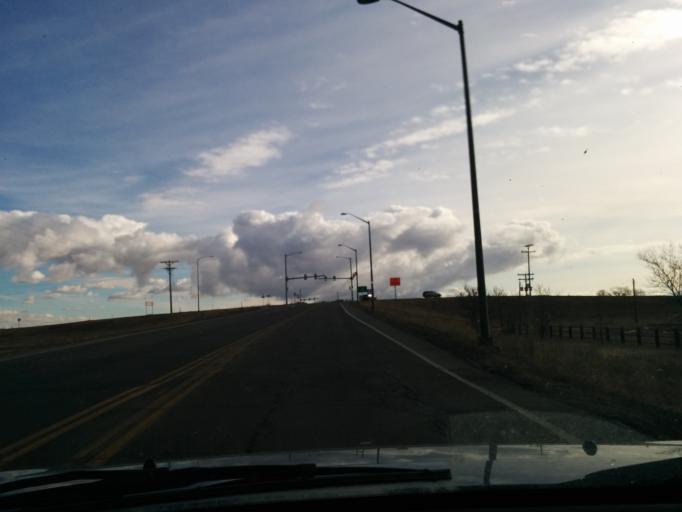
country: US
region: Colorado
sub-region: Larimer County
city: Fort Collins
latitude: 40.5666
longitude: -105.0042
